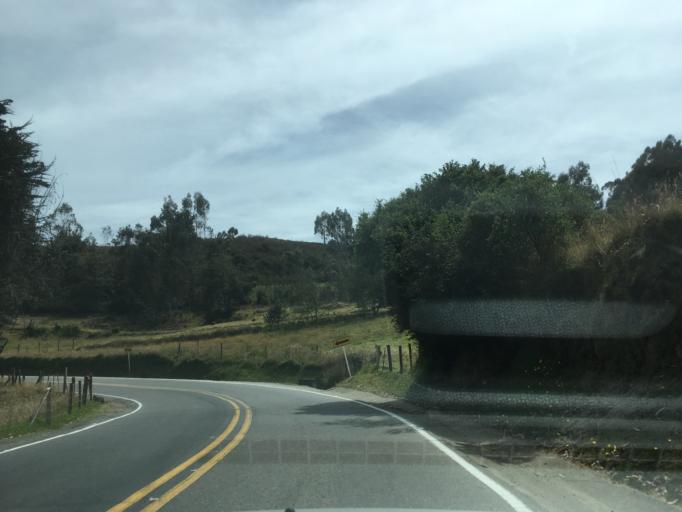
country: CO
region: Boyaca
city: Firavitoba
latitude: 5.6218
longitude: -72.9132
